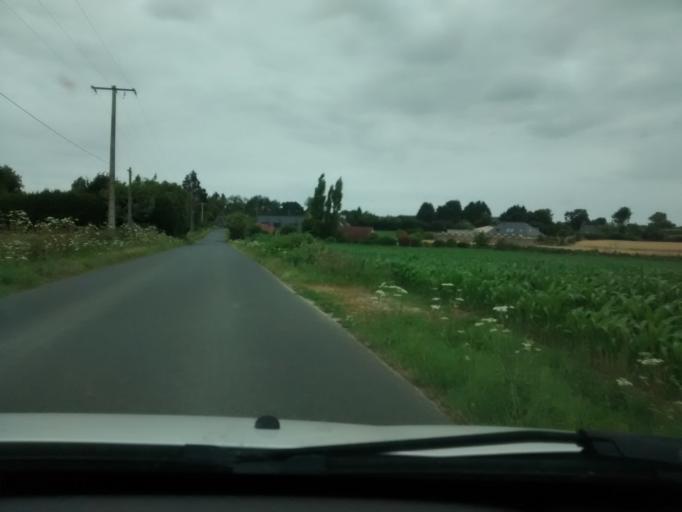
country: FR
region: Brittany
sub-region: Departement des Cotes-d'Armor
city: Trevou-Treguignec
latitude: 48.7898
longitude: -3.3412
